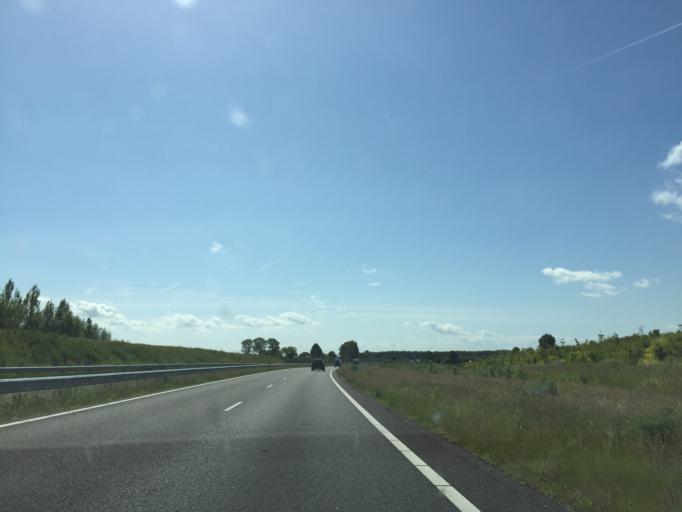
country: NL
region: Zeeland
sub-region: Gemeente Middelburg
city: Middelburg
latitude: 51.5149
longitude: 3.6283
